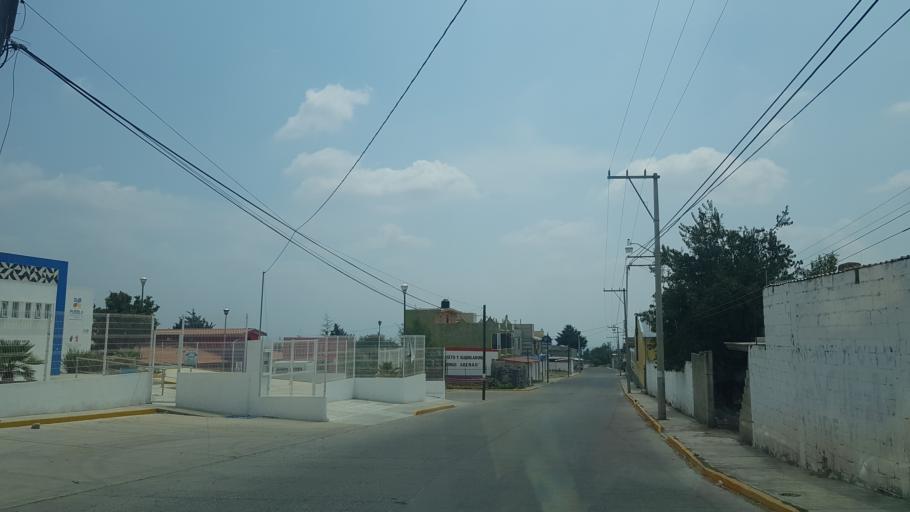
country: MX
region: Puebla
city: Domingo Arenas
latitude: 19.1394
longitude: -98.4494
